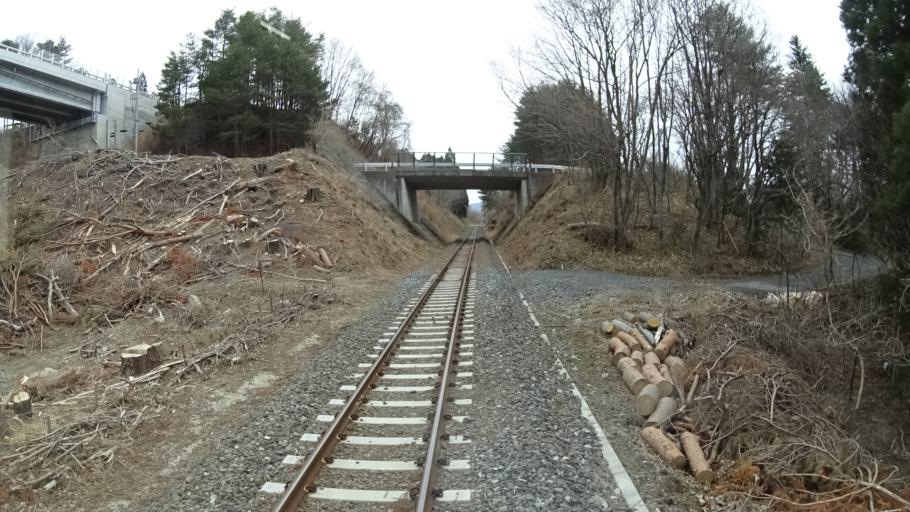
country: JP
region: Iwate
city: Otsuchi
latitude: 39.4011
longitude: 141.9510
